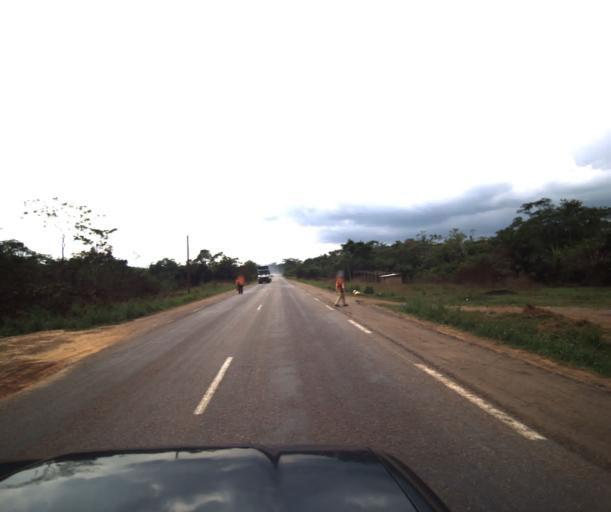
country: CM
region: Littoral
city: Edea
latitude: 3.9487
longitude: 10.0360
